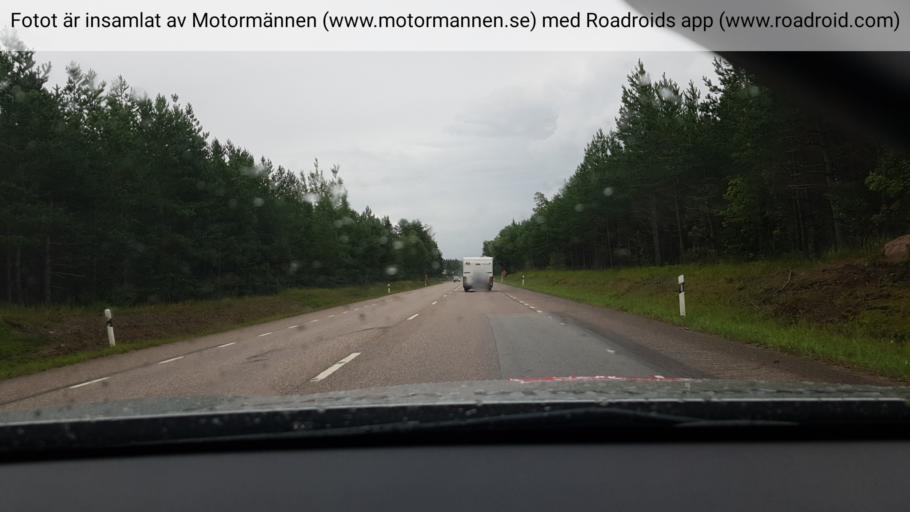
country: SE
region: Uppsala
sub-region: Alvkarleby Kommun
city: AElvkarleby
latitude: 60.6050
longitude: 17.4416
